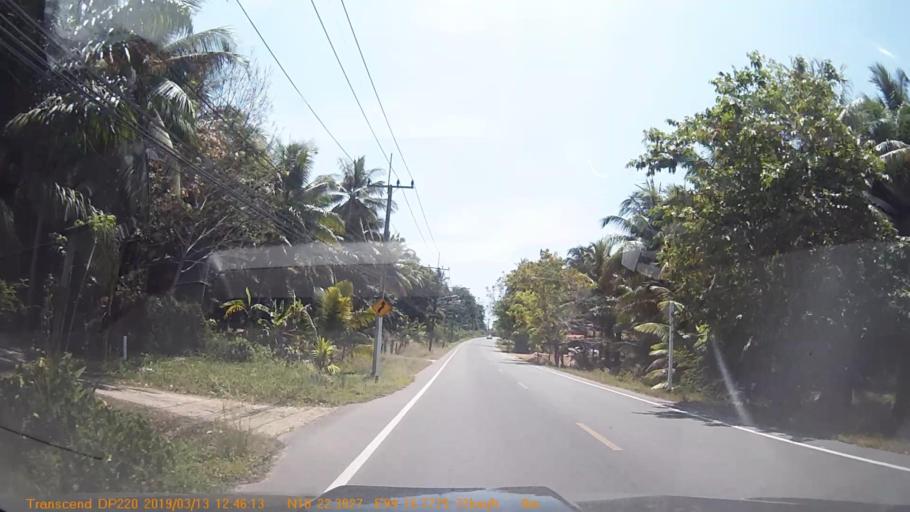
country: TH
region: Chumphon
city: Chumphon
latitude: 10.3727
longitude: 99.2629
